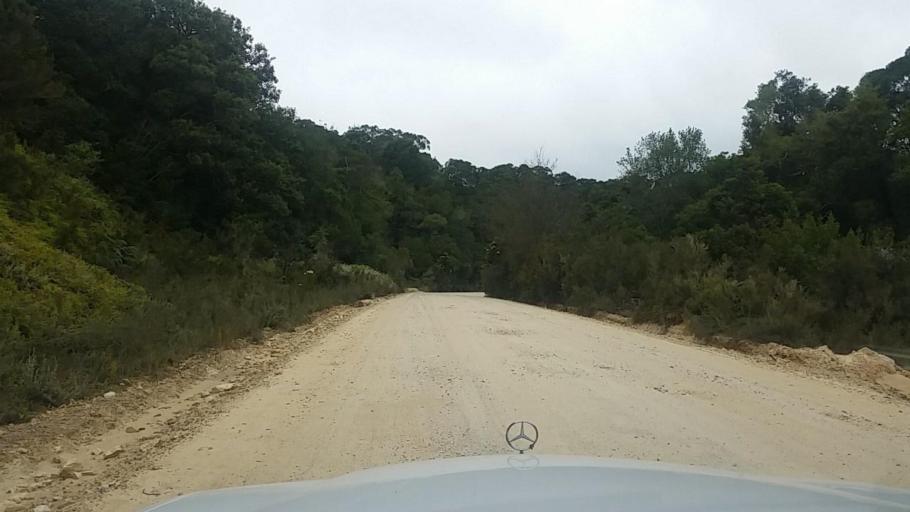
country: ZA
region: Western Cape
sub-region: Eden District Municipality
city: Knysna
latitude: -33.9606
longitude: 23.1587
